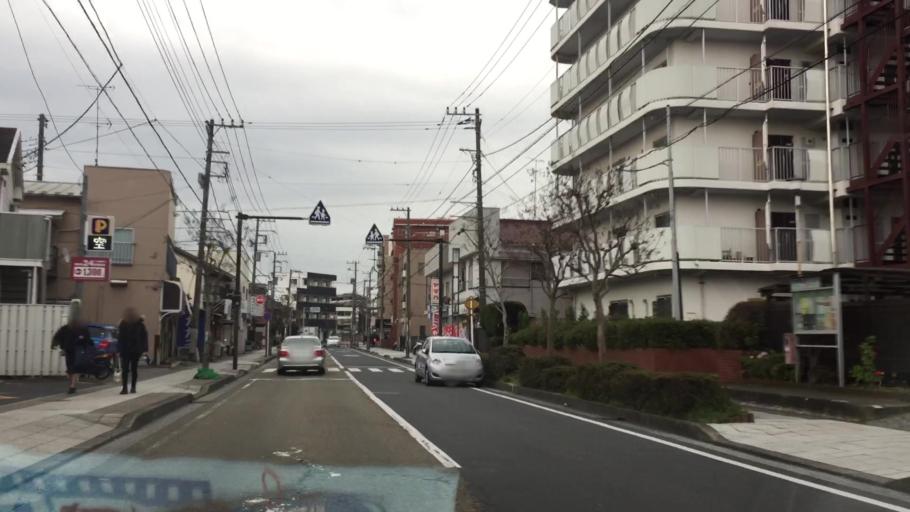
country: JP
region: Kanagawa
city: Zushi
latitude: 35.3403
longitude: 139.6255
